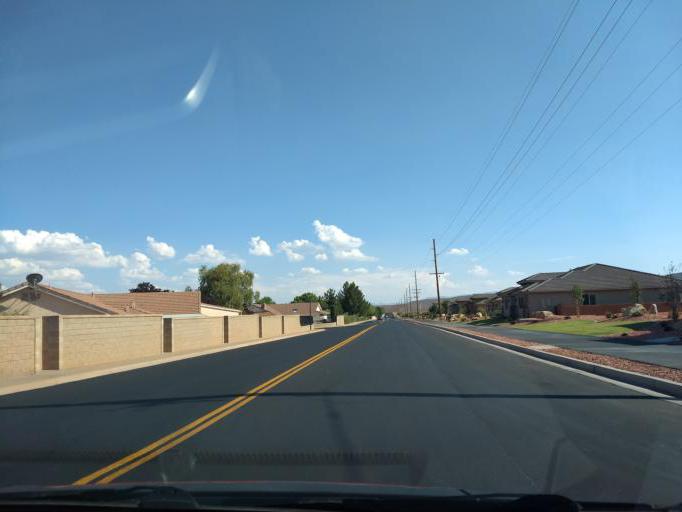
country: US
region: Utah
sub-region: Washington County
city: Ivins
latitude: 37.1572
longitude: -113.6748
